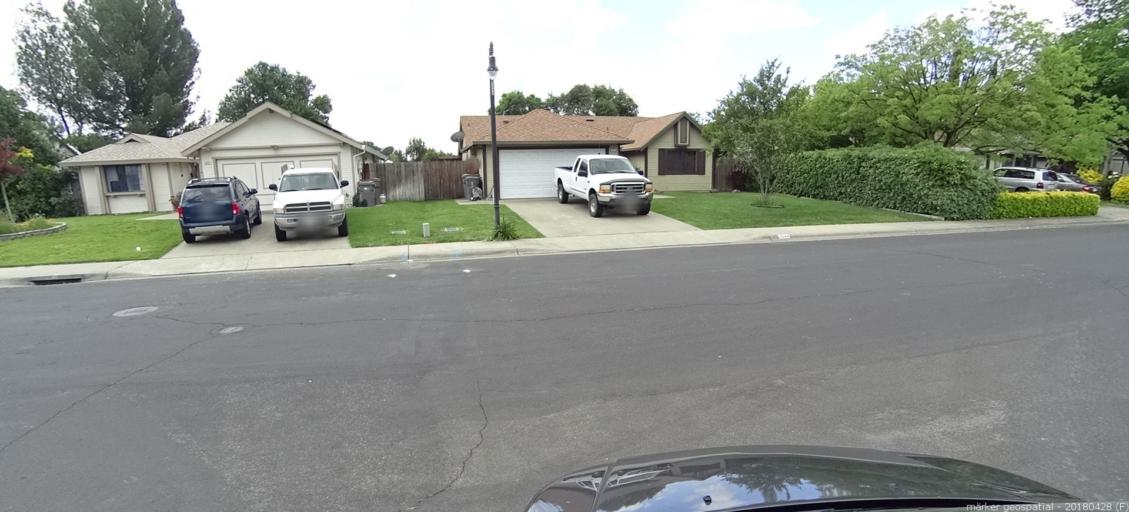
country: US
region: California
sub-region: Yolo County
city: West Sacramento
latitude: 38.5449
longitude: -121.5573
